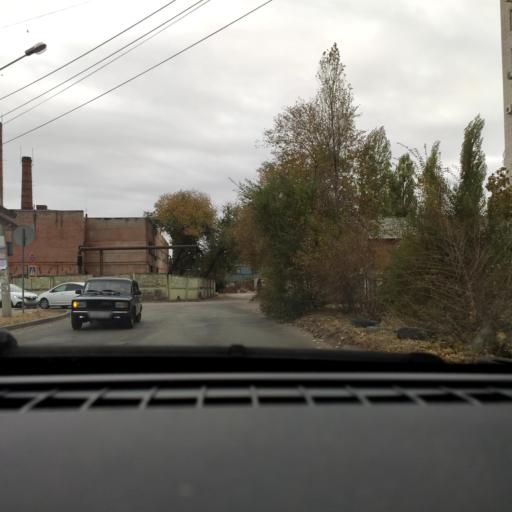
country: RU
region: Voronezj
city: Maslovka
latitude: 51.6357
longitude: 39.2726
